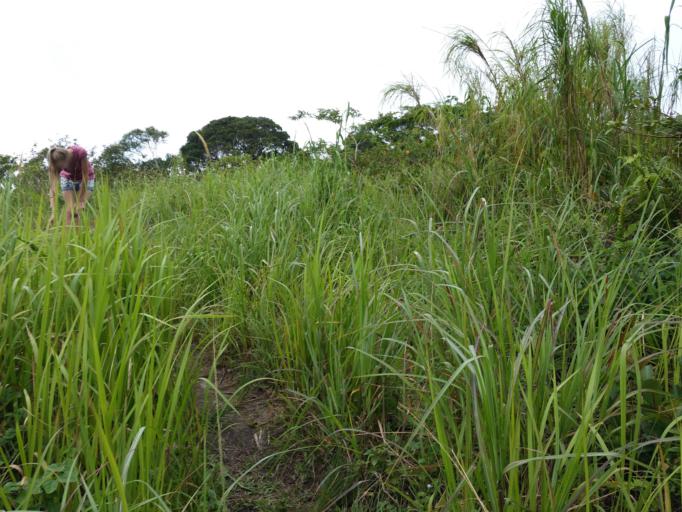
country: KH
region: Kampot
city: Kampot
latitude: 10.6194
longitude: 104.0777
